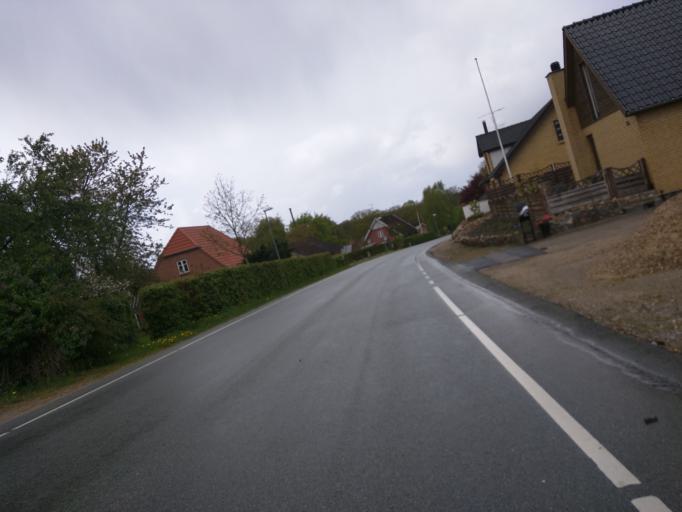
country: DK
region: Central Jutland
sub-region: Viborg Kommune
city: Viborg
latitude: 56.3989
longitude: 9.4357
